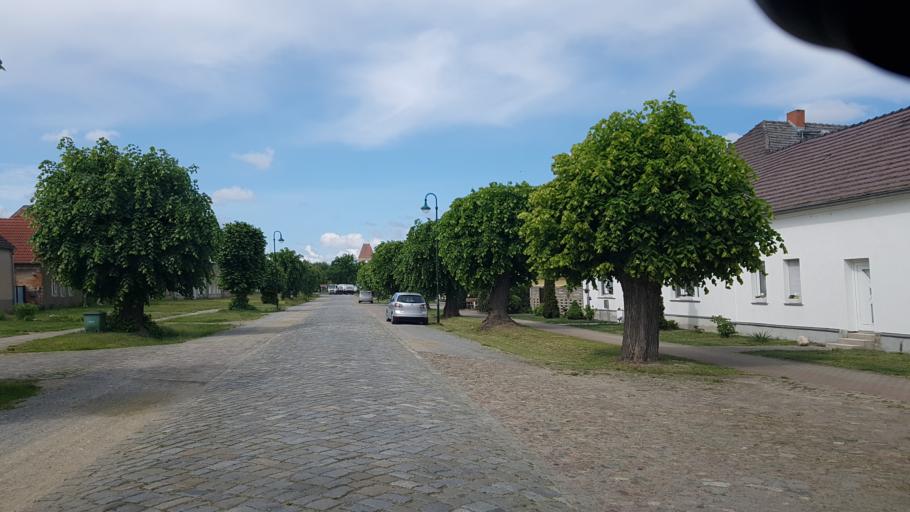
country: DE
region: Brandenburg
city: Luckau
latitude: 51.8198
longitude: 13.7001
